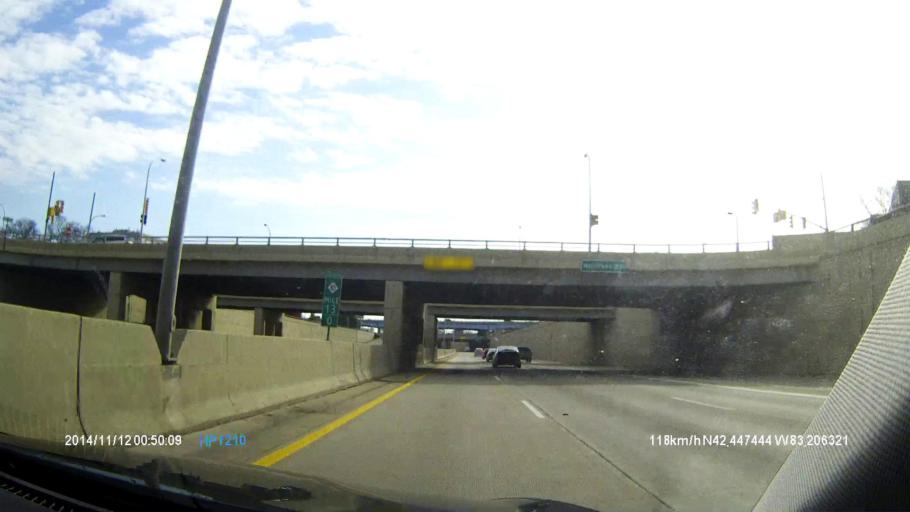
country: US
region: Michigan
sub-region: Oakland County
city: Oak Park
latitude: 42.4471
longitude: -83.2060
